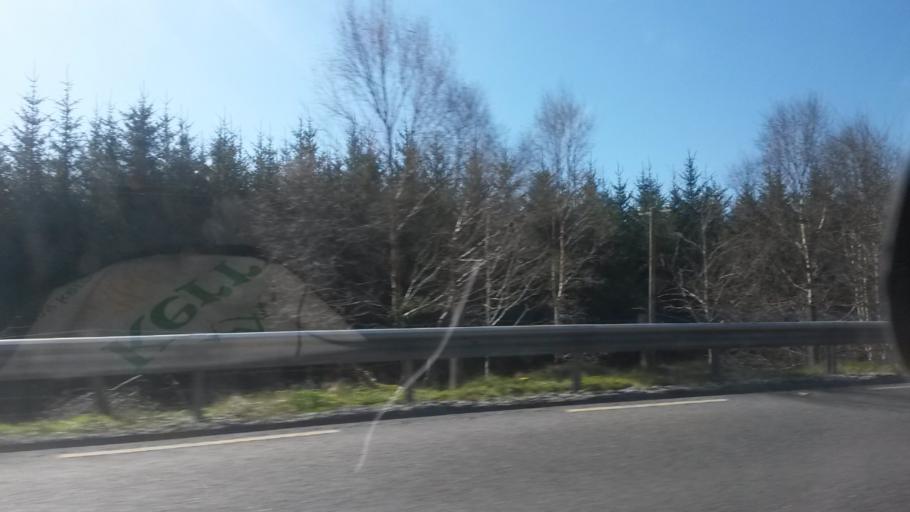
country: IE
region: Munster
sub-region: Ciarrai
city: Cill Airne
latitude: 51.9715
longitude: -9.3462
